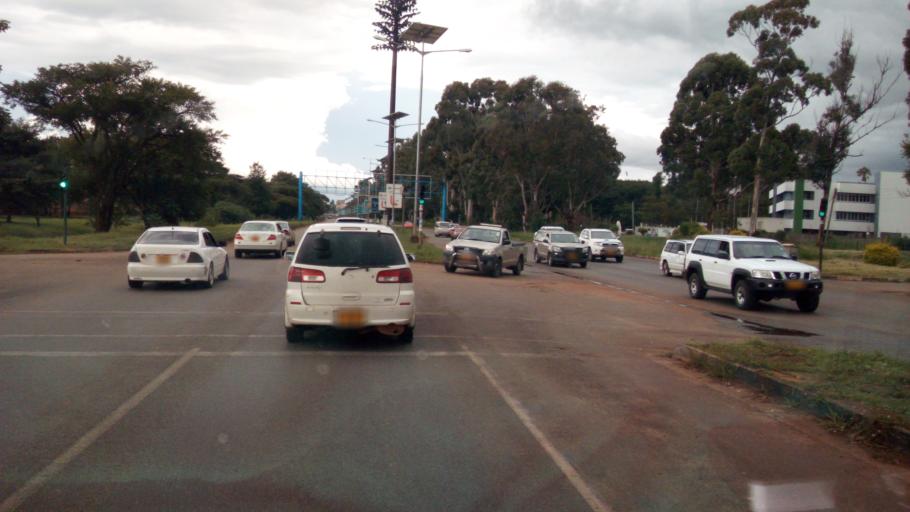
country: ZW
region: Harare
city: Harare
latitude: -17.7836
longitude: 31.0780
